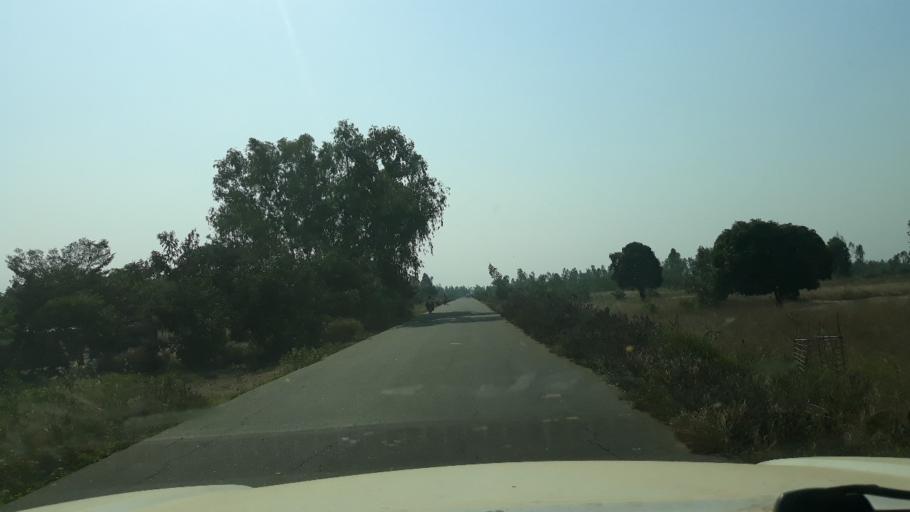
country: BI
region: Cibitoke
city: Cibitoke
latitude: -2.9538
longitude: 29.0748
